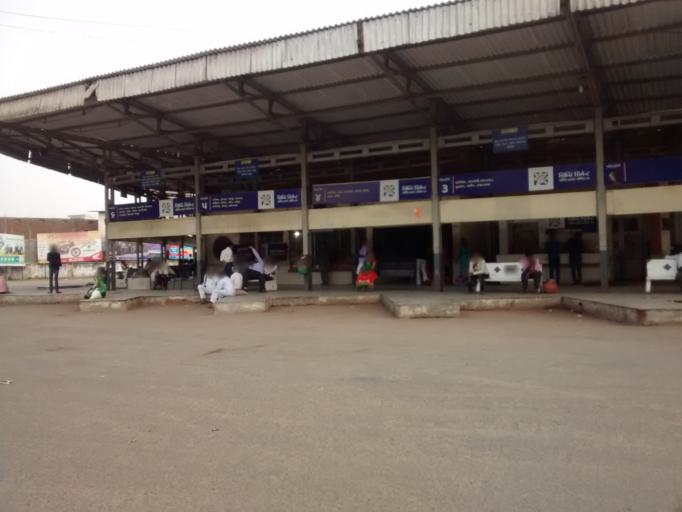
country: IN
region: Gujarat
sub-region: Gandhinagar
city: Dahegam
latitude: 23.1712
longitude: 72.8203
